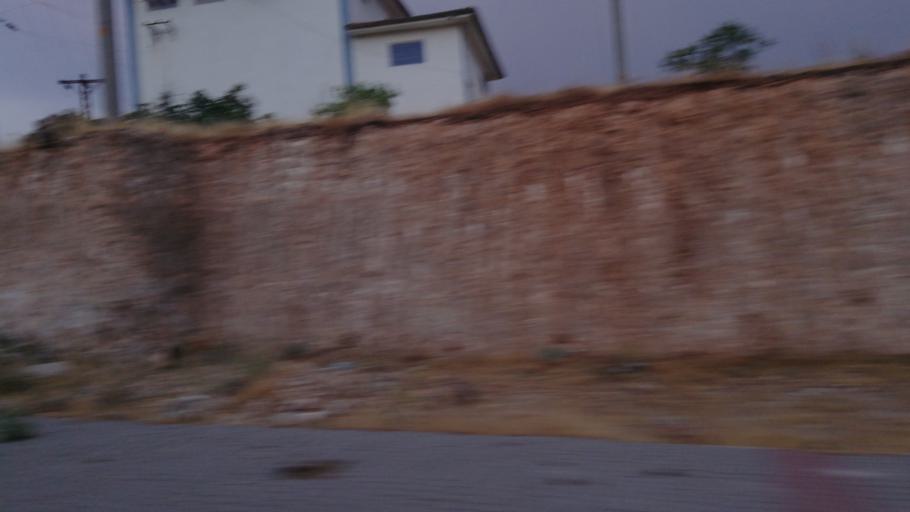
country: TR
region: Mardin
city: Kindirip
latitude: 37.4609
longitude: 41.2253
